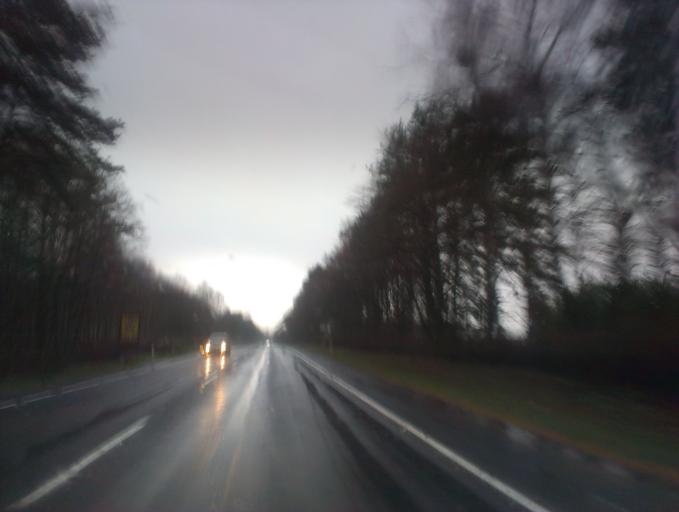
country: PL
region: Greater Poland Voivodeship
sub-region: Powiat pilski
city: Ujscie
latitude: 53.0273
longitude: 16.7985
